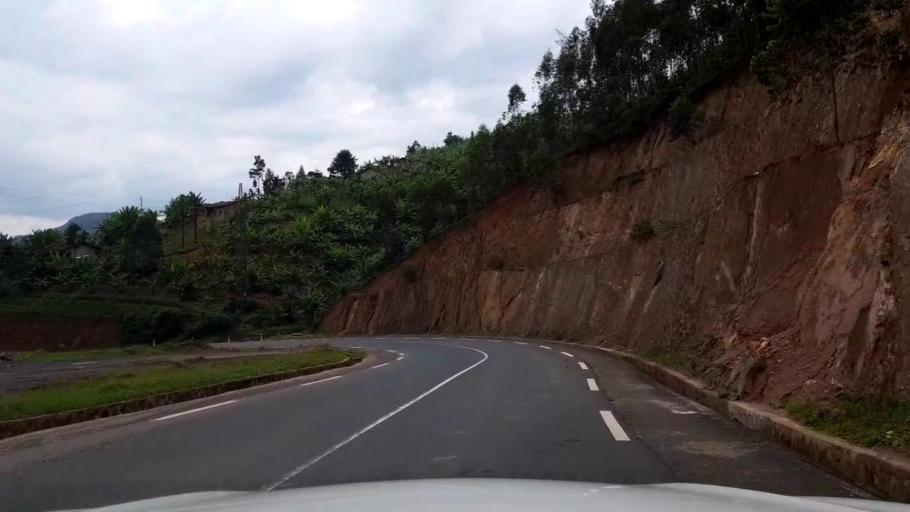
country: RW
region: Western Province
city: Kibuye
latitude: -1.9114
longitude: 29.3691
